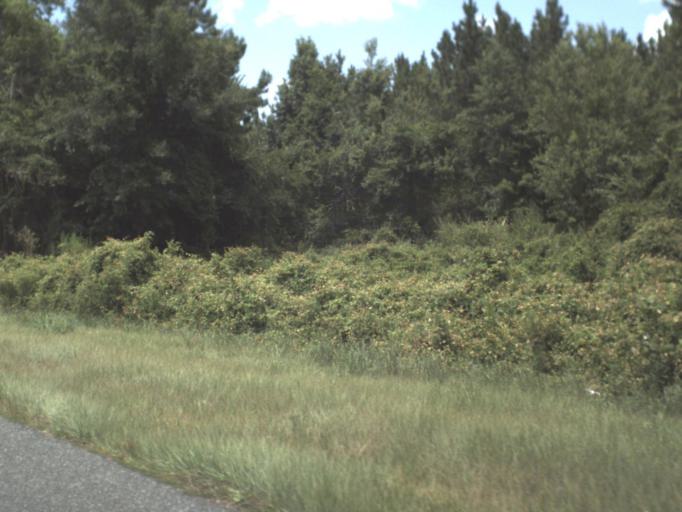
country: US
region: Florida
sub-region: Taylor County
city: Perry
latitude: 30.2314
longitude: -83.6828
